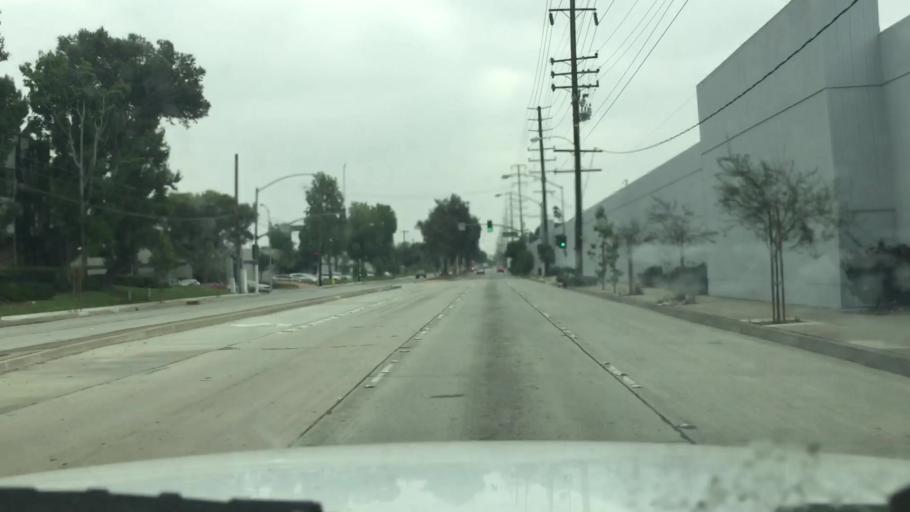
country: US
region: California
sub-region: Los Angeles County
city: Commerce
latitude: 33.9855
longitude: -118.1590
